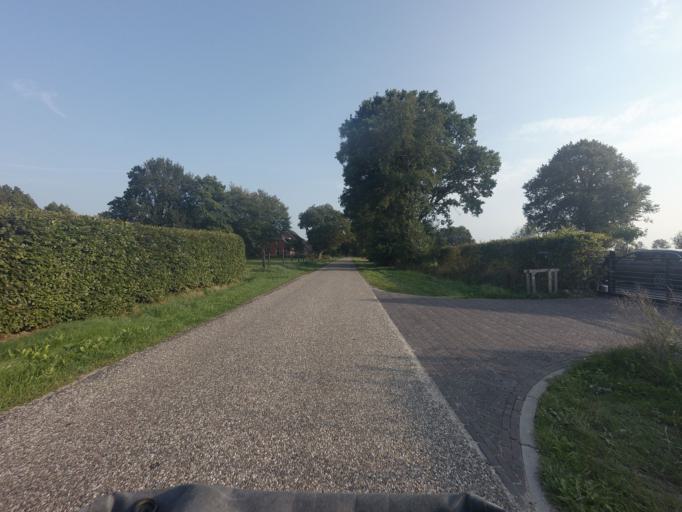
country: NL
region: Drenthe
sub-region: Gemeente Tynaarlo
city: Vries
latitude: 53.1110
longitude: 6.5237
